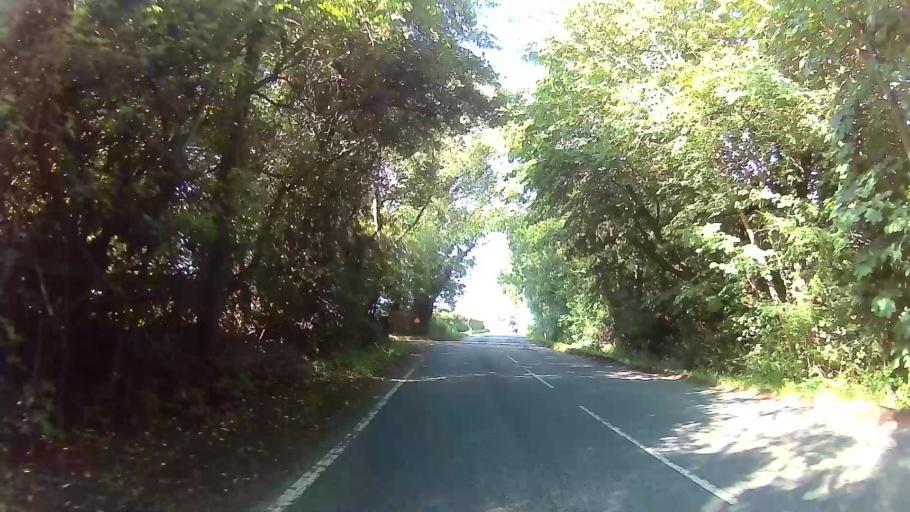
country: GB
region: England
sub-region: Essex
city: Kelvedon Hatch
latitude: 51.6826
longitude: 0.3048
